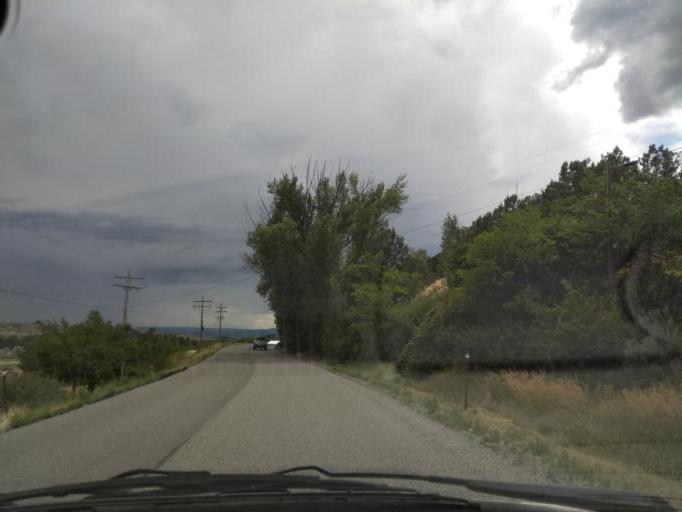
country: US
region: Colorado
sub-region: Delta County
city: Paonia
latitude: 38.8777
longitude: -107.6018
